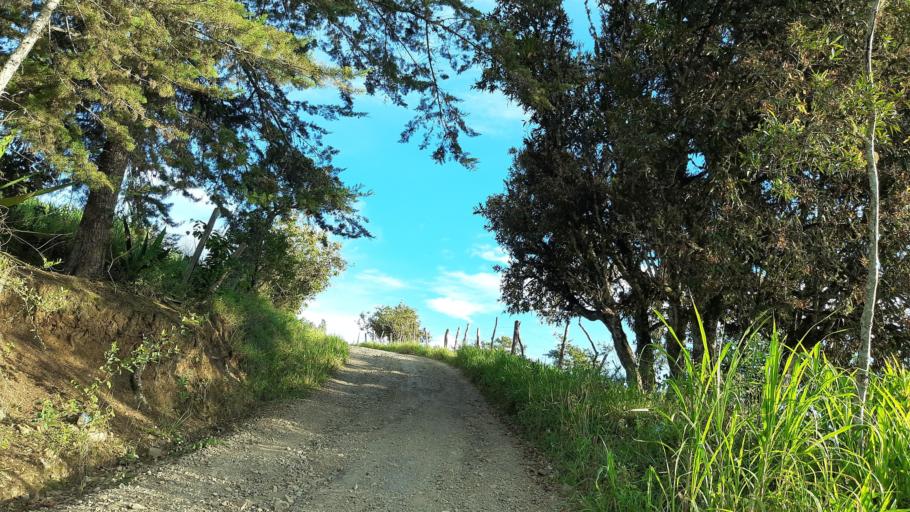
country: CO
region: Boyaca
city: Garagoa
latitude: 5.0662
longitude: -73.3763
